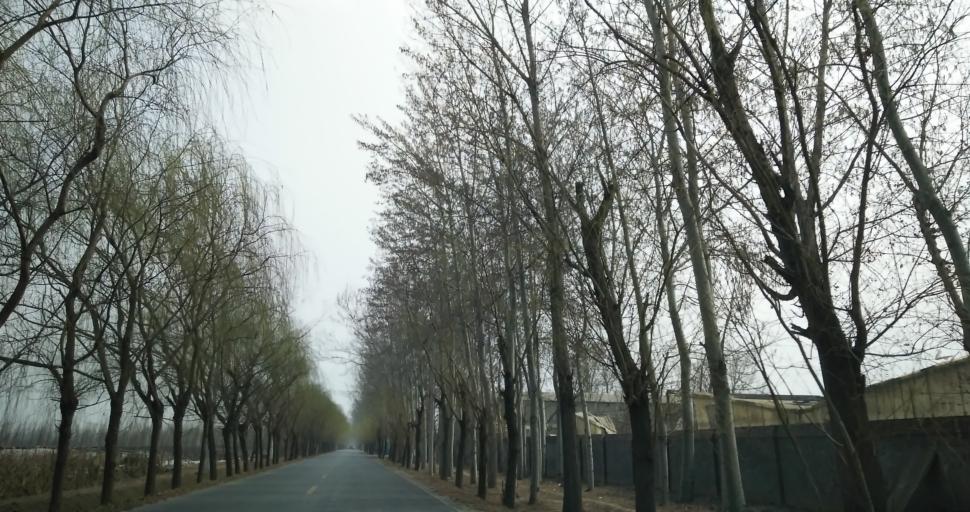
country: CN
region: Beijing
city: Qingyundian
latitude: 39.6983
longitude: 116.4952
